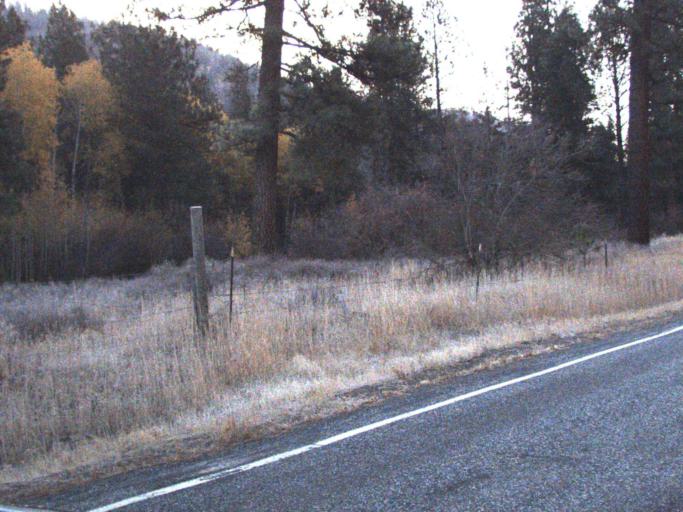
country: US
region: Washington
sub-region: Ferry County
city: Republic
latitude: 48.2994
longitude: -118.7348
